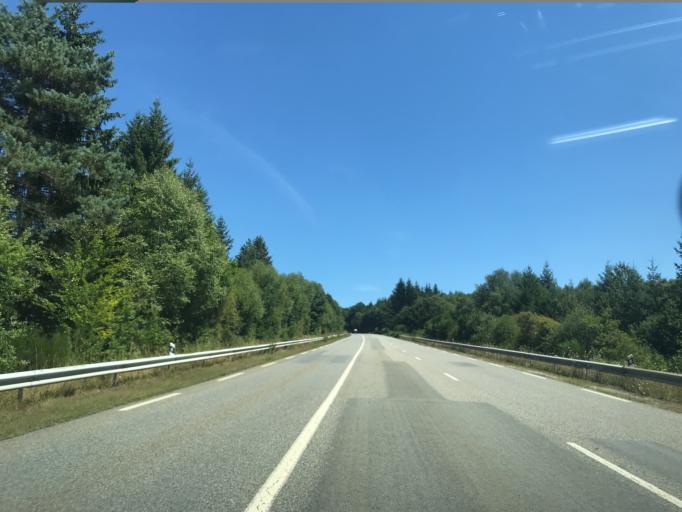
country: FR
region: Limousin
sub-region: Departement de la Correze
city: Meymac
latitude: 45.4709
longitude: 2.1632
